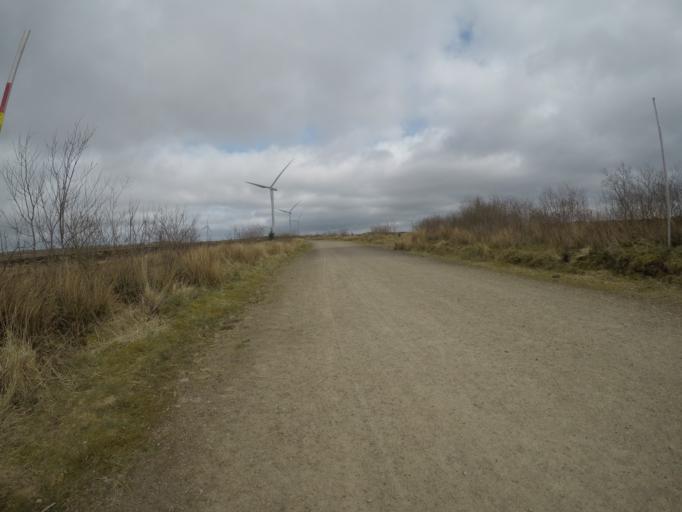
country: GB
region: Scotland
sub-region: East Renfrewshire
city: Newton Mearns
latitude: 55.6979
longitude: -4.3444
